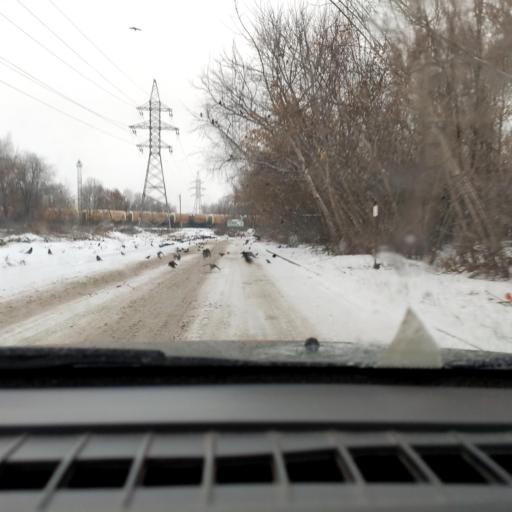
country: RU
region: Samara
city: Tol'yatti
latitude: 53.5622
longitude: 49.3243
